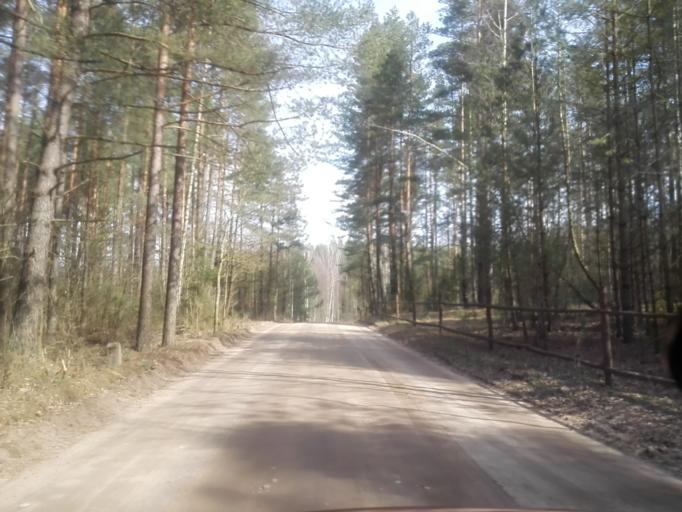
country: PL
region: Podlasie
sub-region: Powiat sejnenski
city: Sejny
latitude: 54.0269
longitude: 23.4122
